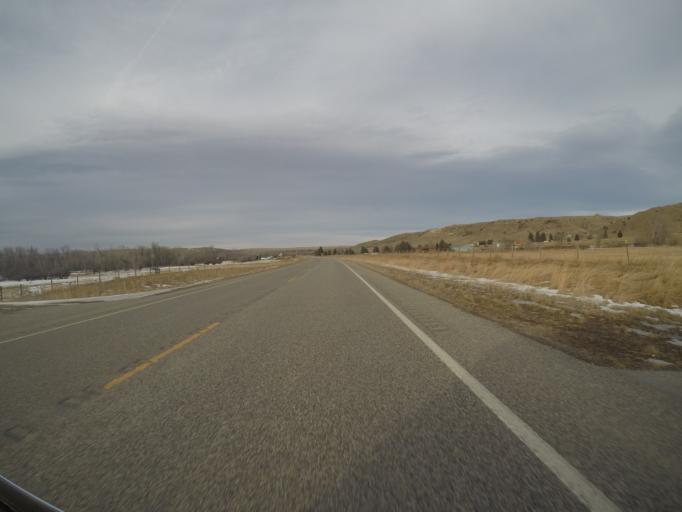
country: US
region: Montana
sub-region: Stillwater County
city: Absarokee
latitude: 45.4762
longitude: -109.4491
